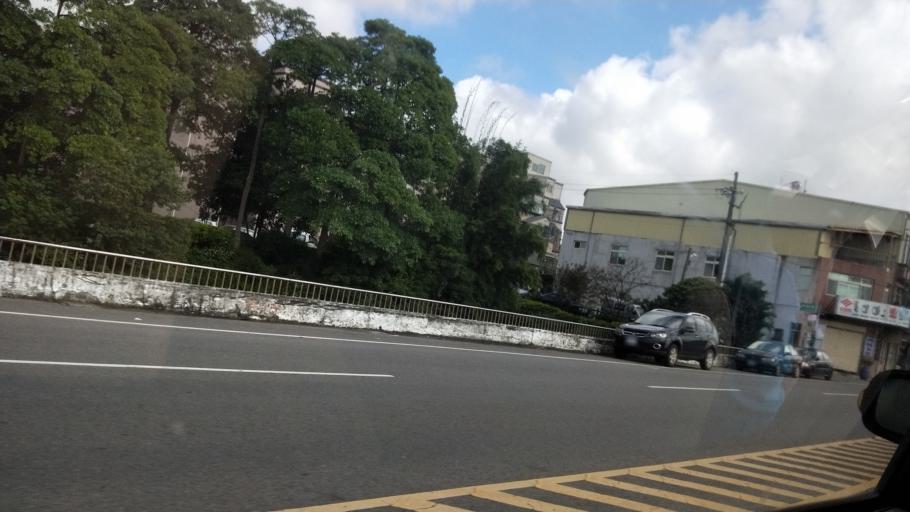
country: TW
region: Taiwan
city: Taoyuan City
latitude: 25.0115
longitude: 121.1355
